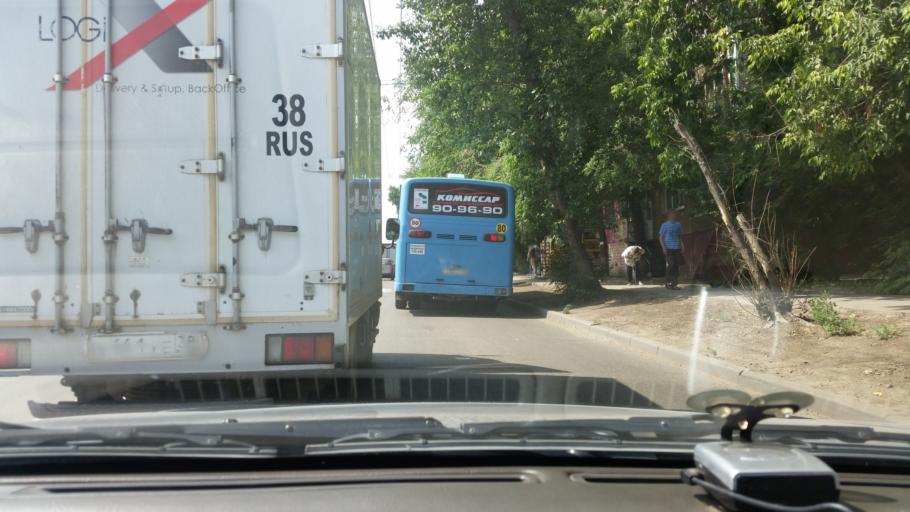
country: RU
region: Irkutsk
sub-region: Irkutskiy Rayon
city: Irkutsk
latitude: 52.2317
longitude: 104.3048
